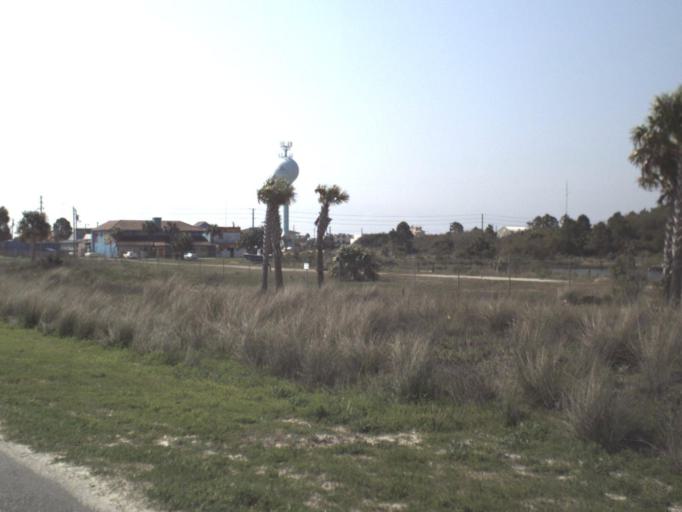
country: US
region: Florida
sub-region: Franklin County
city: Eastpoint
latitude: 29.6666
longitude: -84.8649
